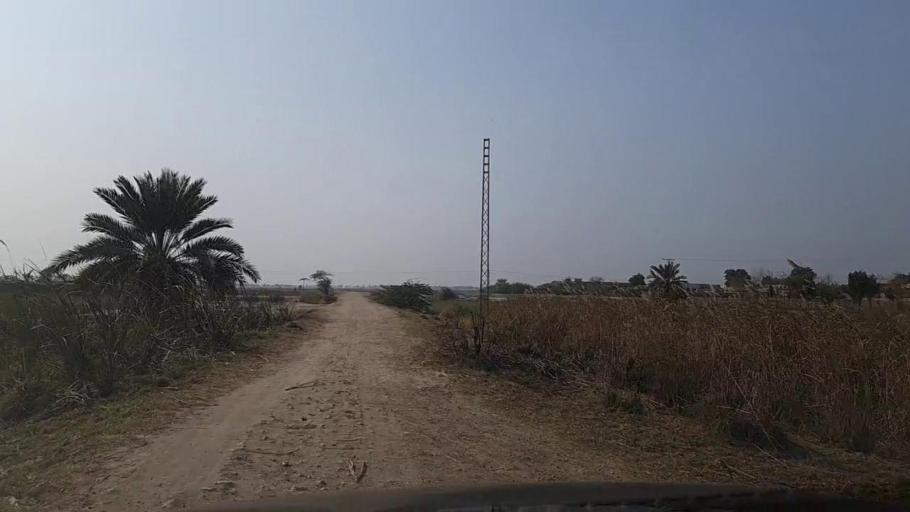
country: PK
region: Sindh
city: Daur
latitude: 26.3914
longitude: 68.4211
